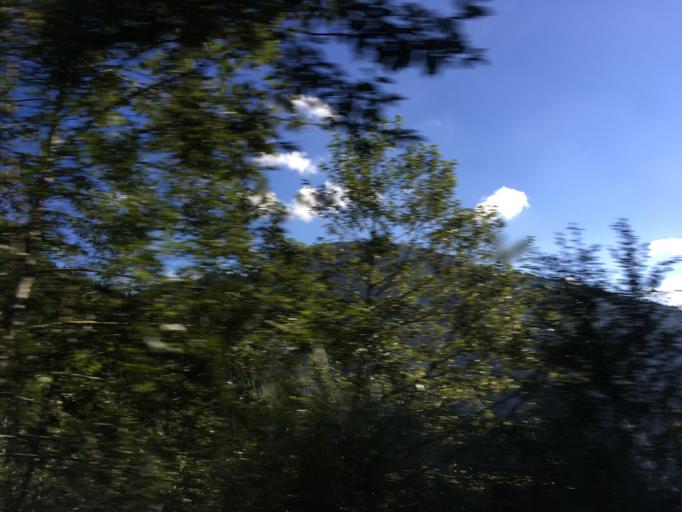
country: TW
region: Taiwan
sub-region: Yilan
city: Yilan
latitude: 24.4948
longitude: 121.5520
